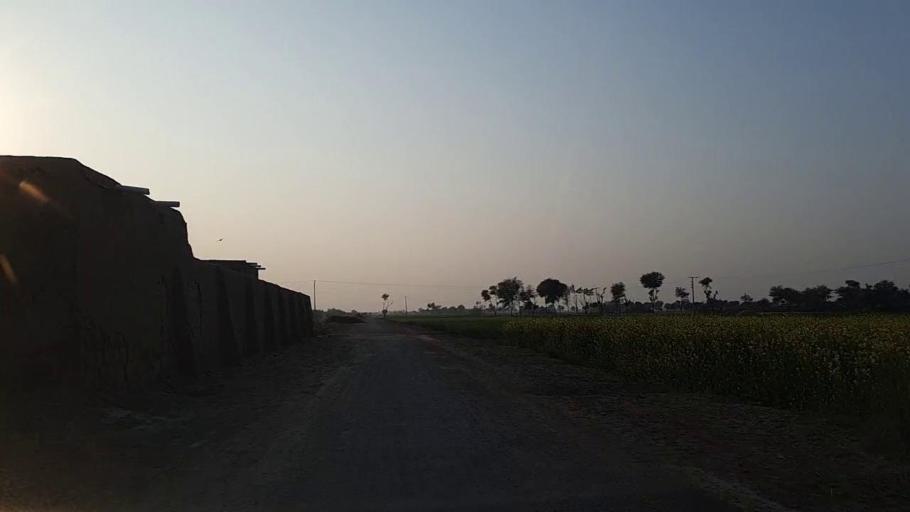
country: PK
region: Sindh
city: Daur
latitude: 26.4164
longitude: 68.3837
